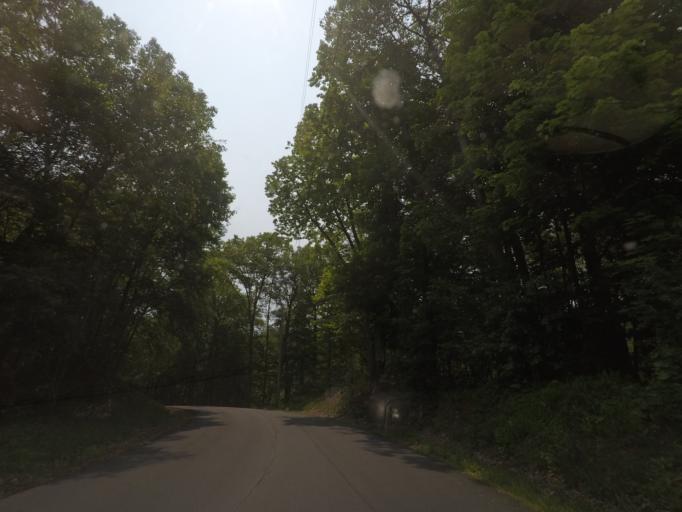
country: US
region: New York
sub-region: Rensselaer County
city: East Greenbush
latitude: 42.5490
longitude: -73.6926
